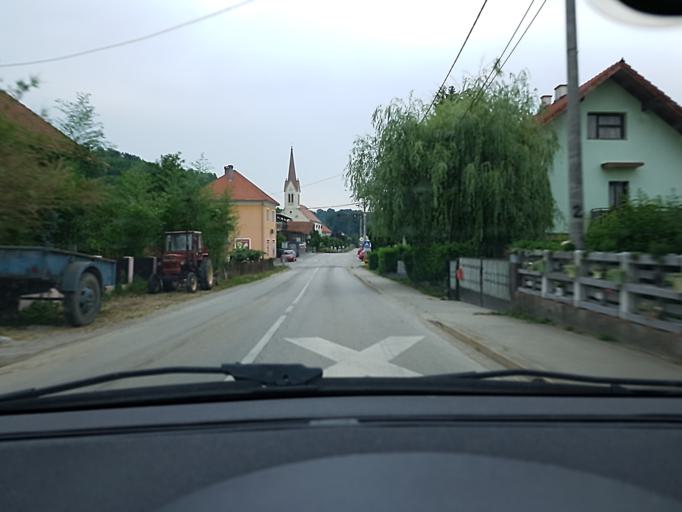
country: HR
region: Zagrebacka
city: Jakovlje
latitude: 45.9585
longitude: 15.8190
